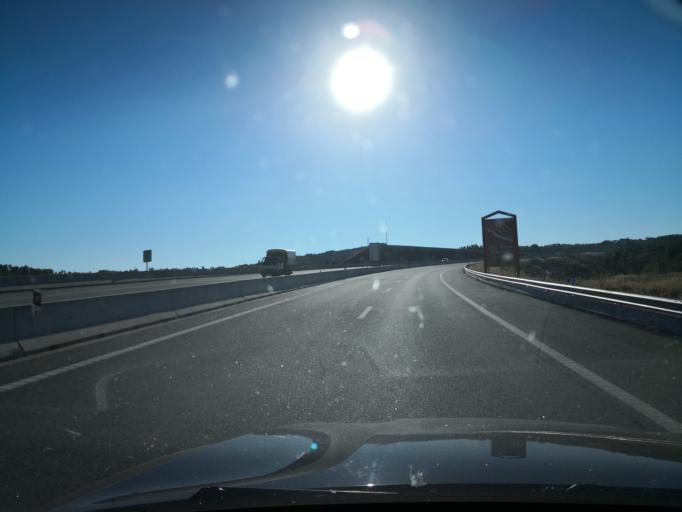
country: PT
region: Vila Real
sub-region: Murca
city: Murca
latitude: 41.3784
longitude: -7.4894
